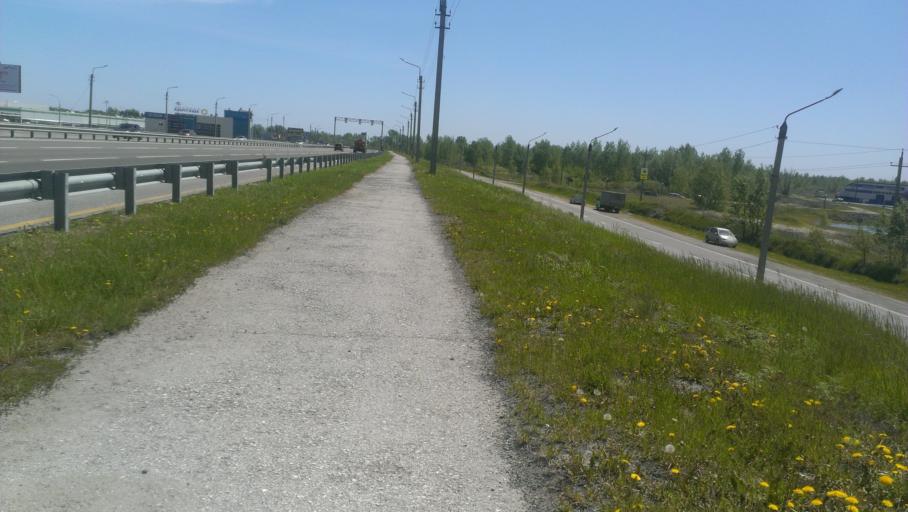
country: RU
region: Altai Krai
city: Zaton
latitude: 53.3176
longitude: 83.8200
